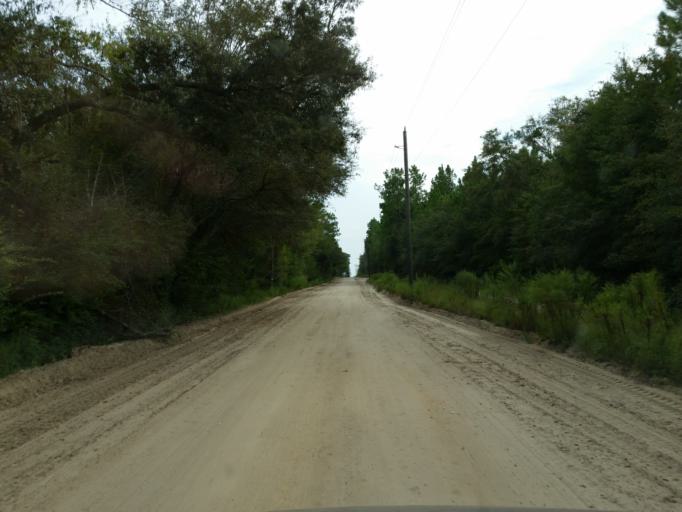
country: US
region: Florida
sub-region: Madison County
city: Madison
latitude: 30.5151
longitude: -83.2200
